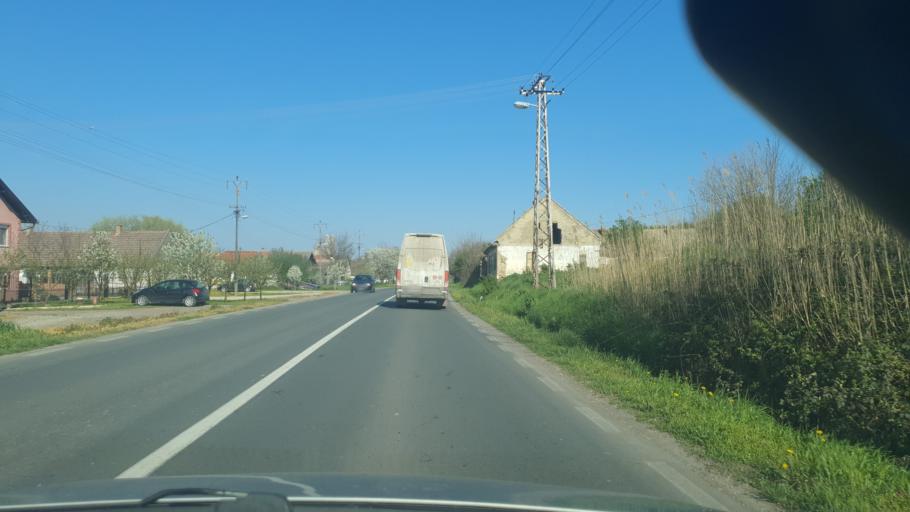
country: RS
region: Autonomna Pokrajina Vojvodina
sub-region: Zapadnobacki Okrug
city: Kula
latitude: 45.6869
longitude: 19.3923
